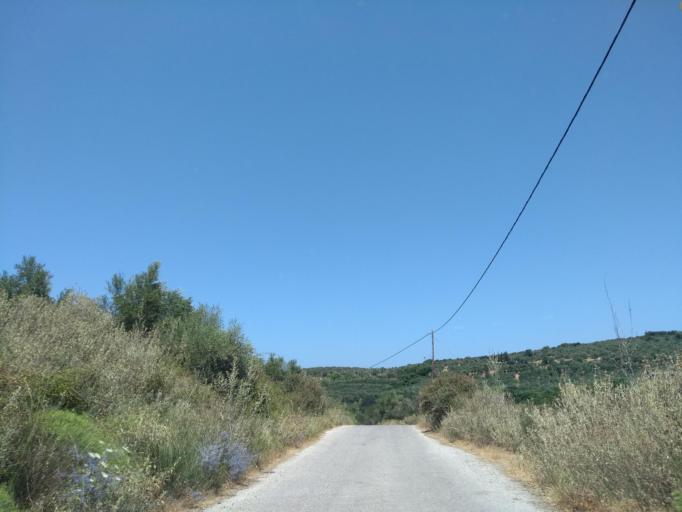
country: GR
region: Crete
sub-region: Nomos Chanias
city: Georgioupolis
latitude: 35.3287
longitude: 24.3201
